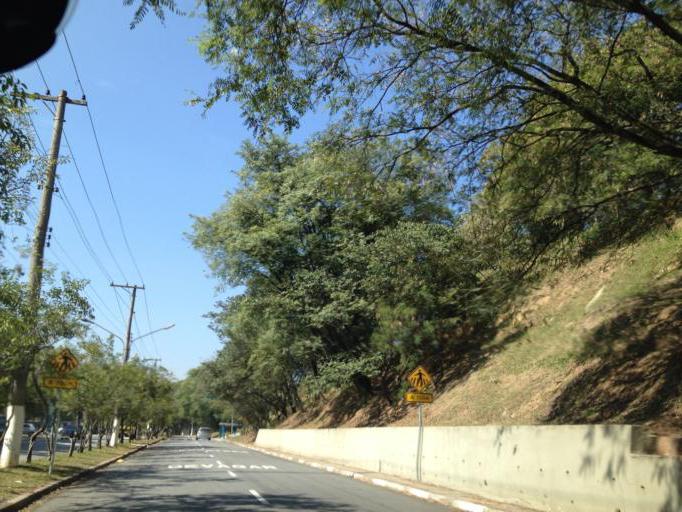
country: BR
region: Sao Paulo
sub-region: Osasco
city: Osasco
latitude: -23.5598
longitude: -46.7405
